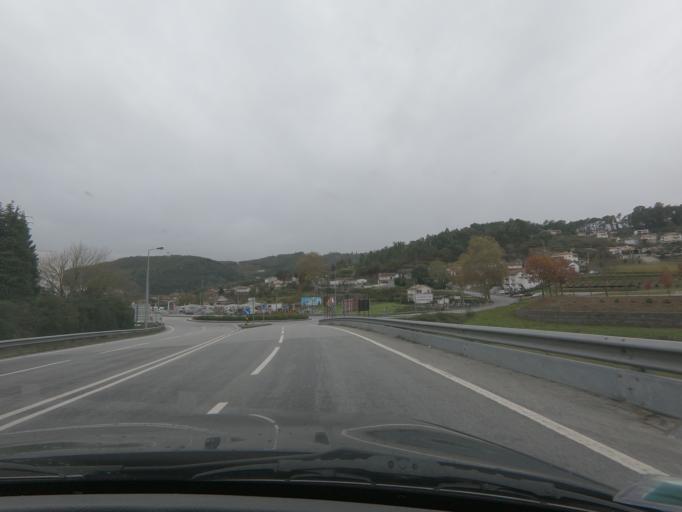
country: PT
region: Porto
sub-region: Amarante
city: Teloes
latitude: 41.2939
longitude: -8.0976
